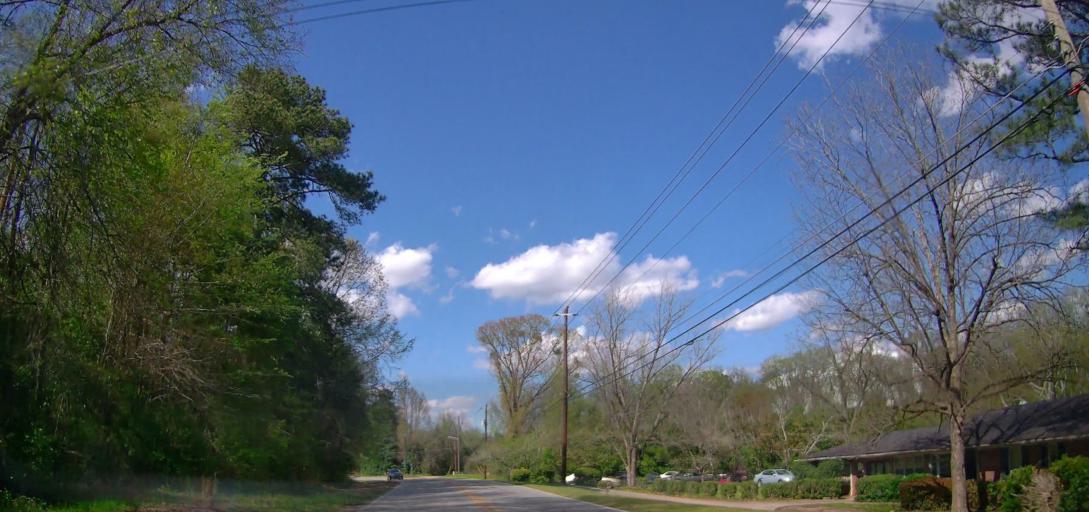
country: US
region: Georgia
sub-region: Bibb County
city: Macon
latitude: 32.8315
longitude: -83.5621
